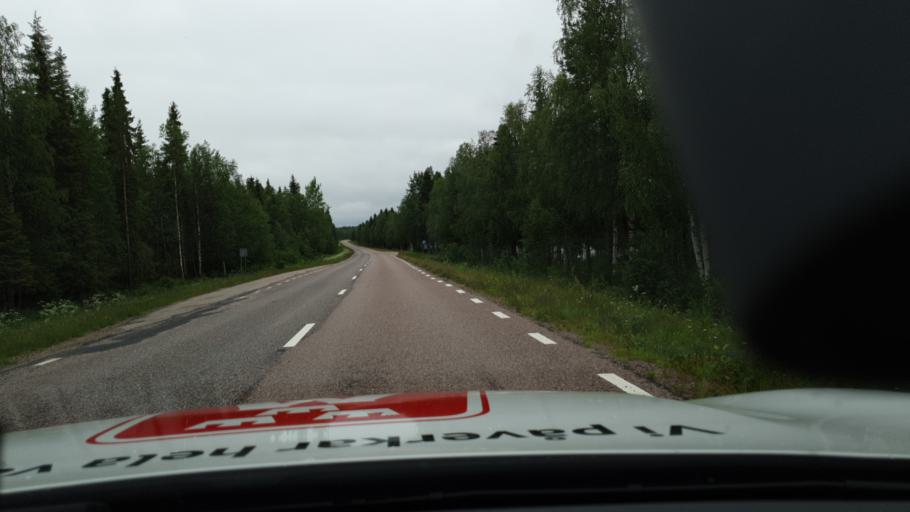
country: FI
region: Lapland
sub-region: Tunturi-Lappi
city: Kolari
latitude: 67.0612
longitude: 23.6724
